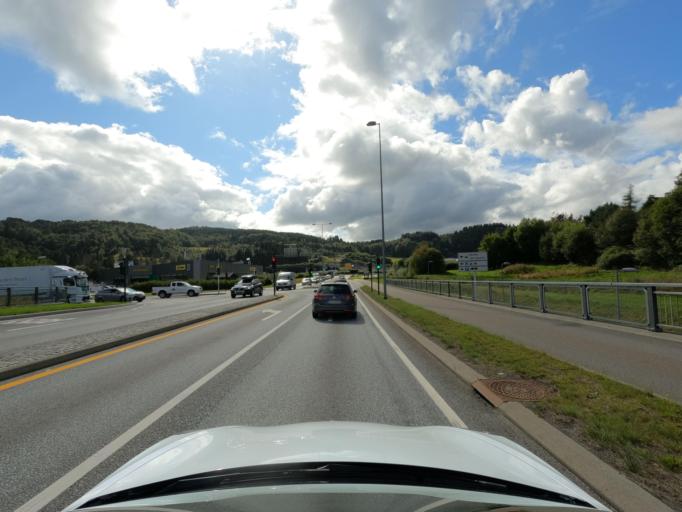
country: NO
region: Hordaland
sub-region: Bergen
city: Hylkje
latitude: 60.4846
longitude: 5.3752
